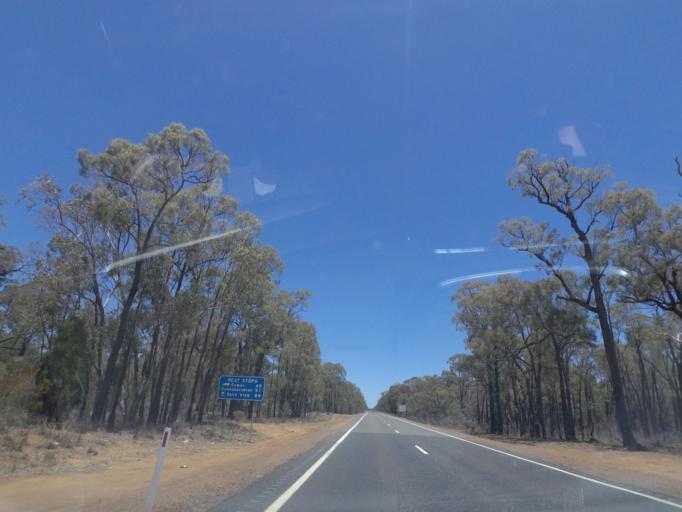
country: AU
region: New South Wales
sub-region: Warrumbungle Shire
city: Coonabarabran
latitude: -30.8575
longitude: 149.4555
